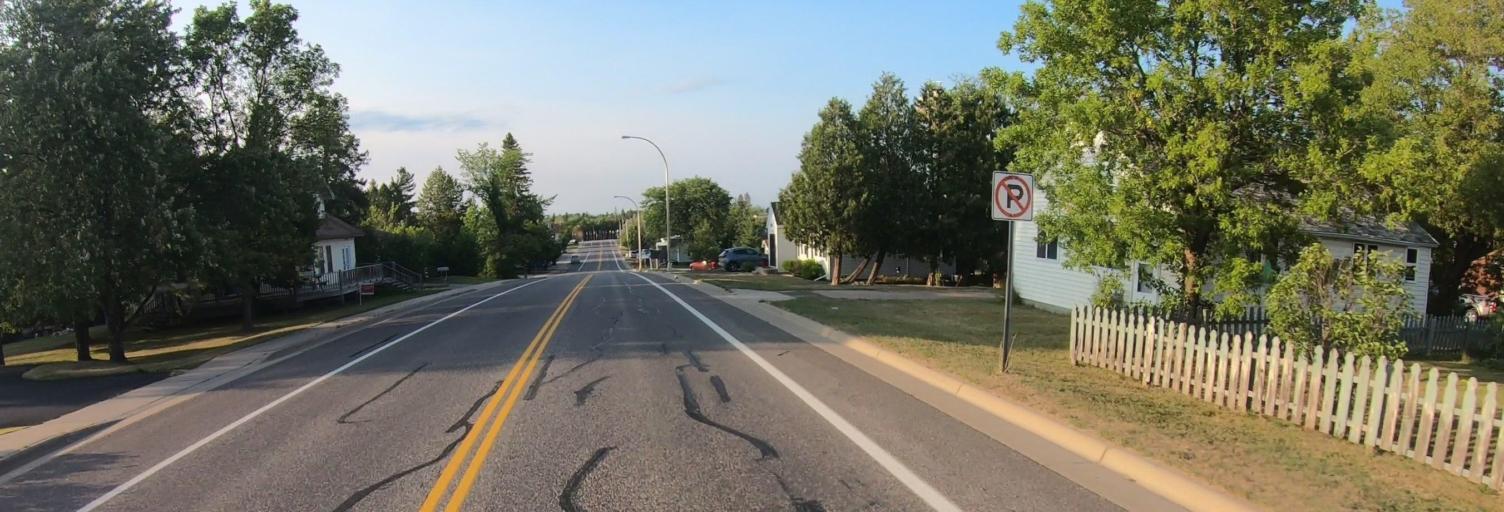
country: US
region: Minnesota
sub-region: Saint Louis County
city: Mountain Iron
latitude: 47.8487
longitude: -92.6810
